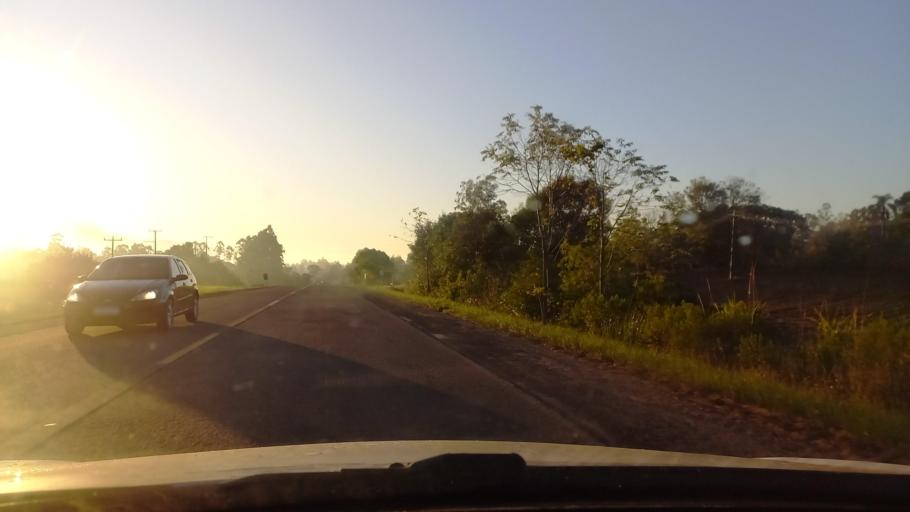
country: BR
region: Rio Grande do Sul
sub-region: Candelaria
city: Candelaria
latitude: -29.6807
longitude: -52.8287
